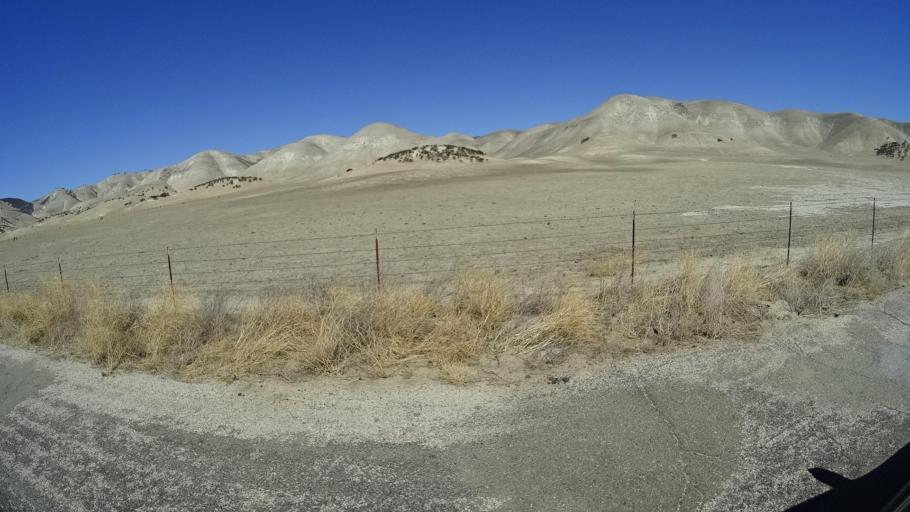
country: US
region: California
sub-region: Monterey County
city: King City
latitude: 36.2924
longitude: -120.9785
